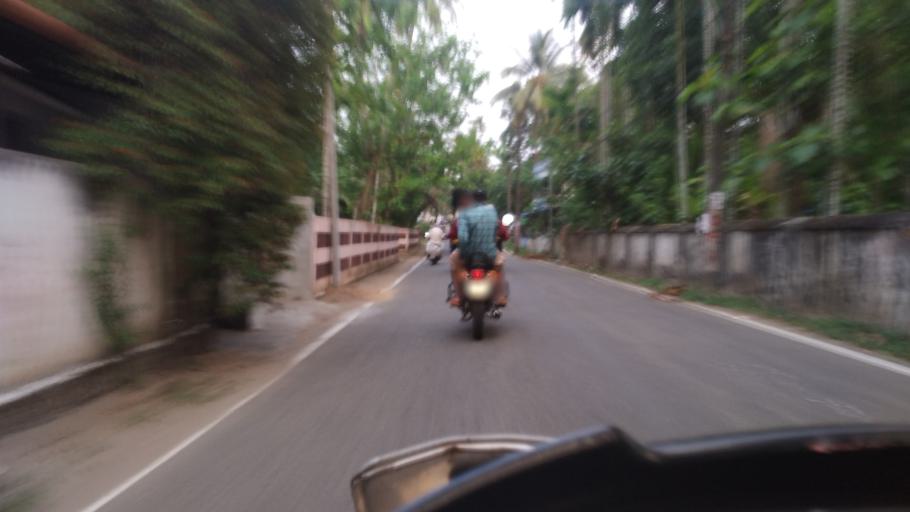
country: IN
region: Kerala
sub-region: Thrissur District
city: Kodungallur
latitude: 10.1648
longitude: 76.2053
